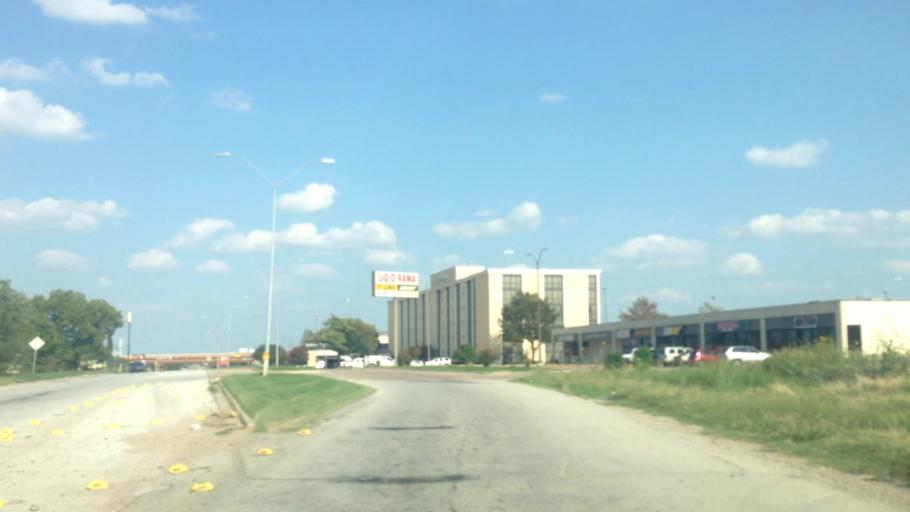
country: US
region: Texas
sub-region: Tarrant County
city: Blue Mound
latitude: 32.8244
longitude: -97.3175
